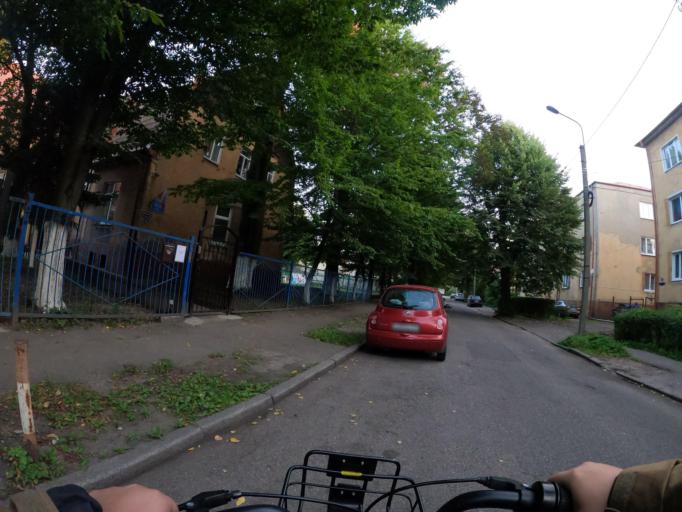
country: RU
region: Kaliningrad
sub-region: Gorod Kaliningrad
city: Kaliningrad
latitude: 54.7155
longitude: 20.4623
